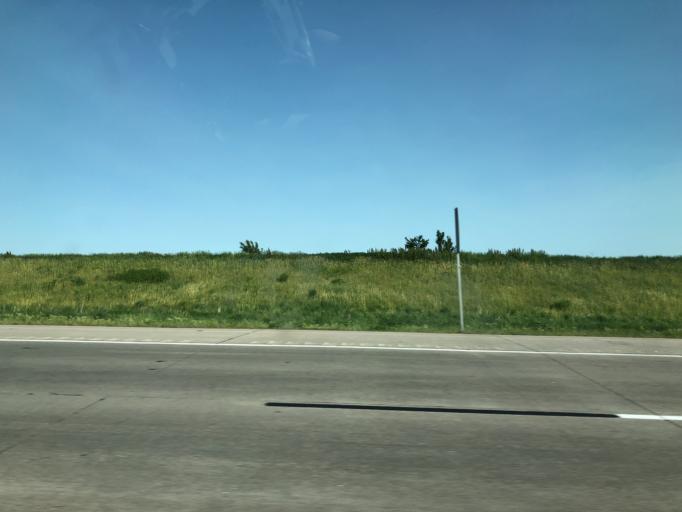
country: US
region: Nebraska
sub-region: Lancaster County
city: Waverly
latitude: 40.9334
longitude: -96.4379
